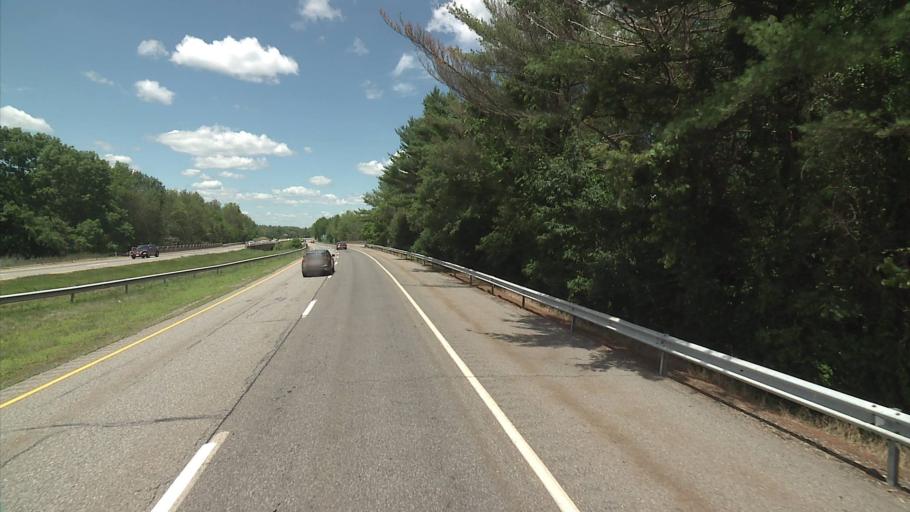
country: US
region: Connecticut
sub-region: Windham County
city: Killingly Center
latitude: 41.8366
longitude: -71.8756
